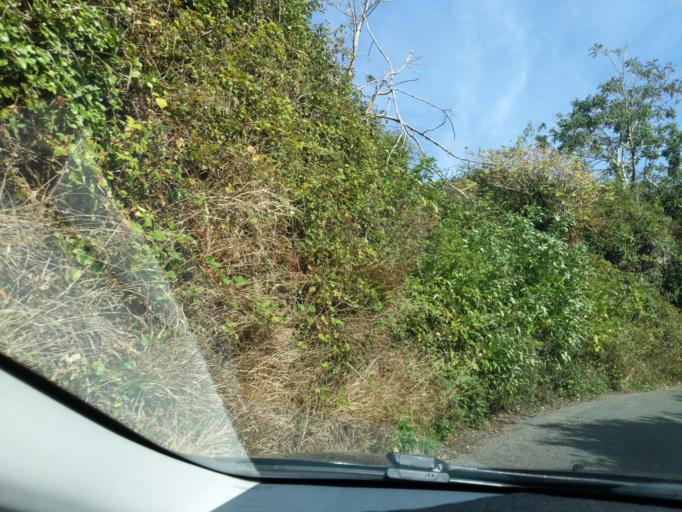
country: GB
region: England
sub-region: Cornwall
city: Torpoint
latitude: 50.3555
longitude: -4.2227
